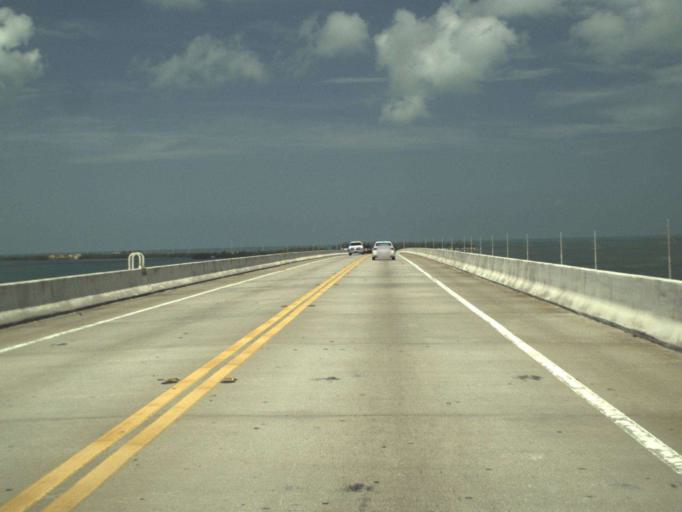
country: US
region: Florida
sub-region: Monroe County
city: Islamorada
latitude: 24.8380
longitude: -80.7733
